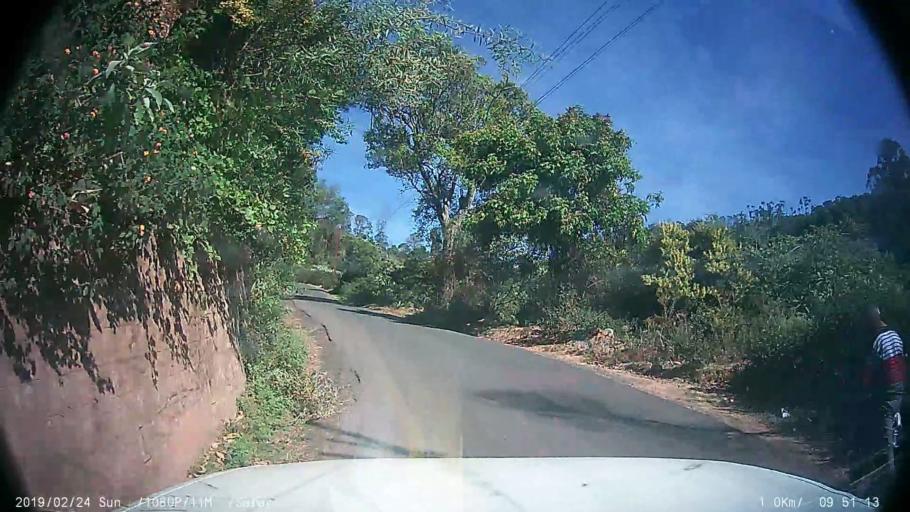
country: IN
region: Tamil Nadu
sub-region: Nilgiri
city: Wellington
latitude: 11.3512
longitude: 76.7754
